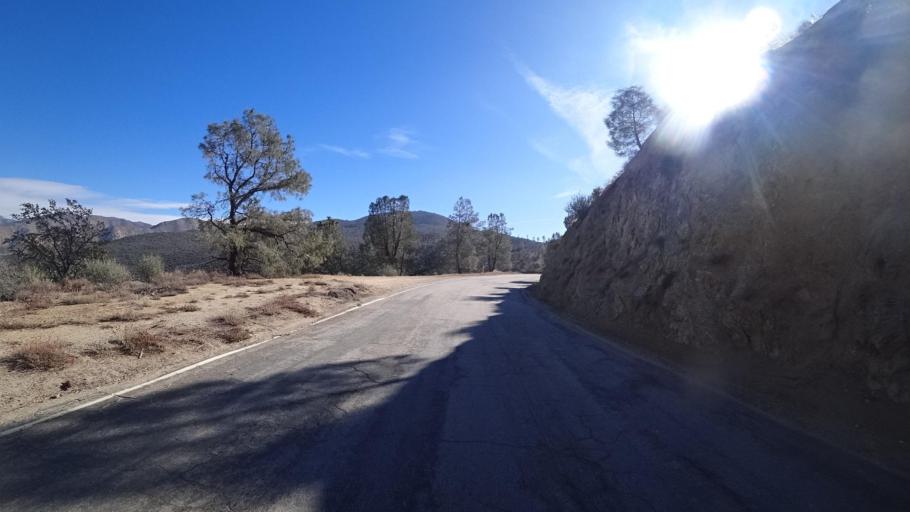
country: US
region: California
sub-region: Kern County
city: Bodfish
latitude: 35.5804
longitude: -118.5050
